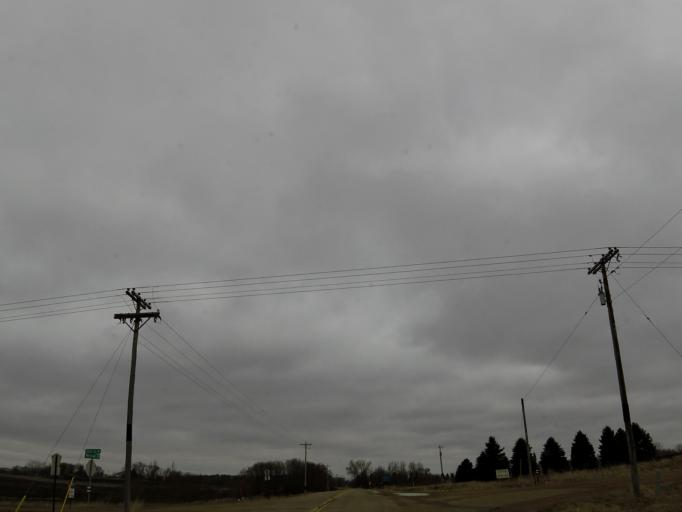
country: US
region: Minnesota
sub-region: Scott County
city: Jordan
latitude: 44.7035
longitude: -93.5414
